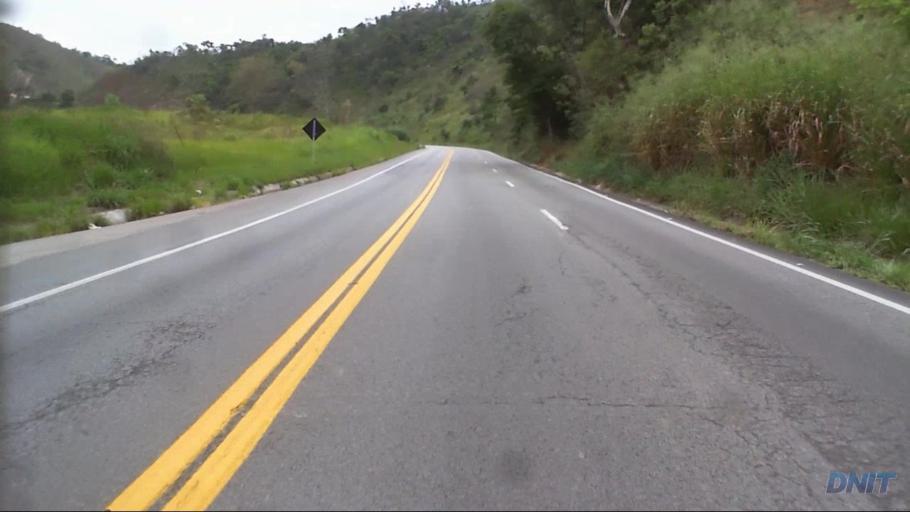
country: BR
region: Minas Gerais
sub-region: Nova Era
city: Nova Era
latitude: -19.6325
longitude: -42.8982
